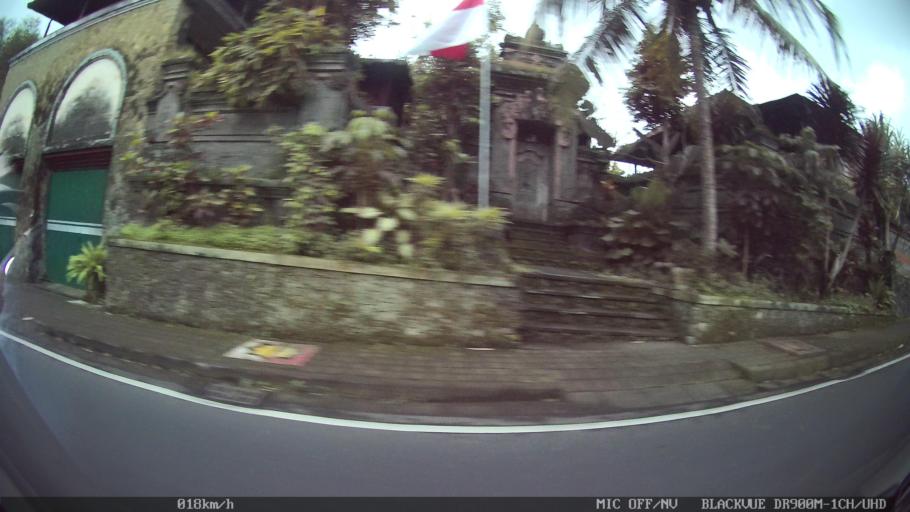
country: ID
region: Bali
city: Banjar Tebongkang
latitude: -8.5312
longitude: 115.2311
